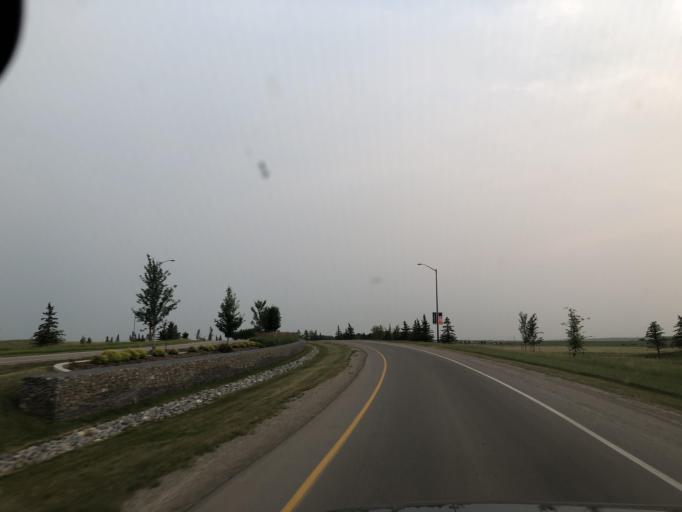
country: CA
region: Alberta
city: Cochrane
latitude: 51.1083
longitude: -114.3919
